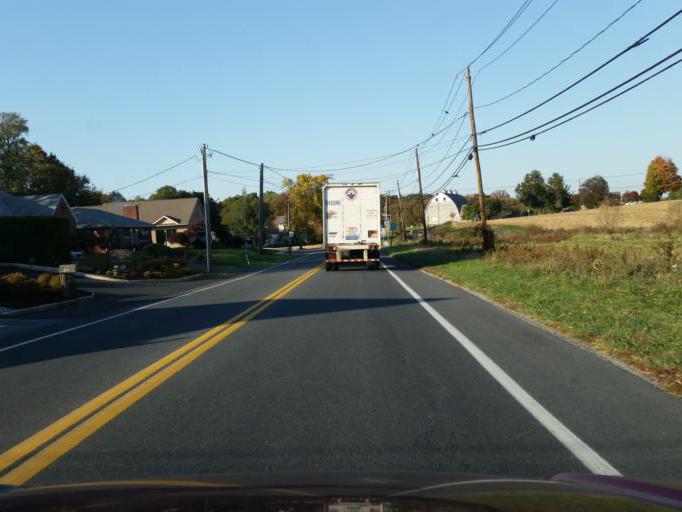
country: US
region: Pennsylvania
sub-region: Dauphin County
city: Hershey
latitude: 40.2724
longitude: -76.6482
